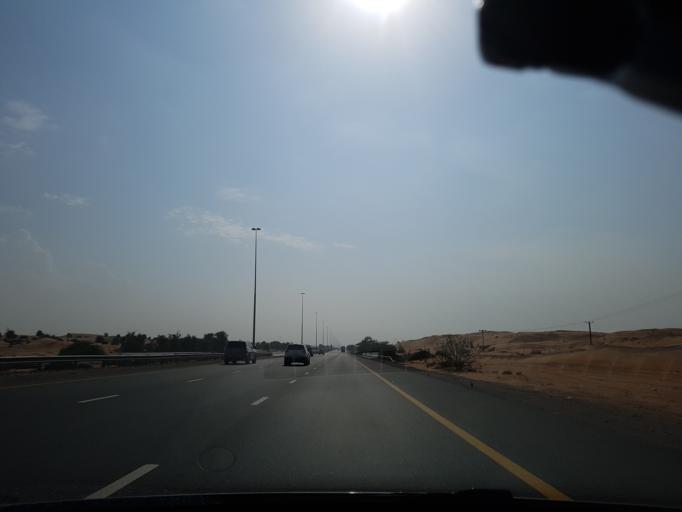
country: AE
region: Umm al Qaywayn
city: Umm al Qaywayn
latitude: 25.5123
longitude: 55.7050
